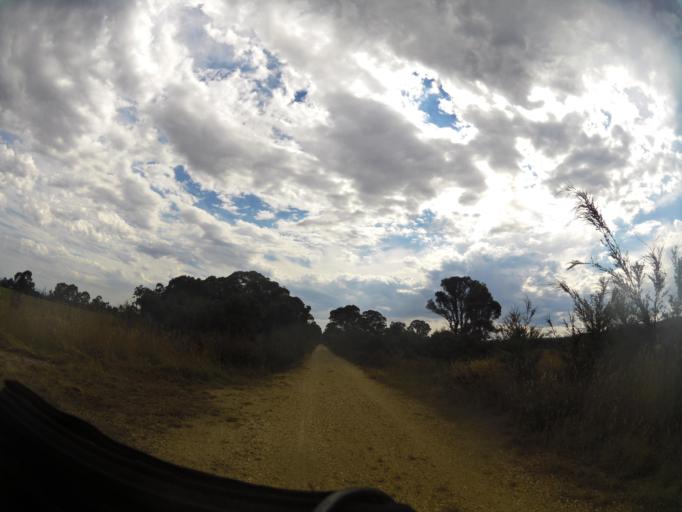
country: AU
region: Victoria
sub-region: Wellington
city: Heyfield
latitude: -38.0431
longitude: 146.6427
